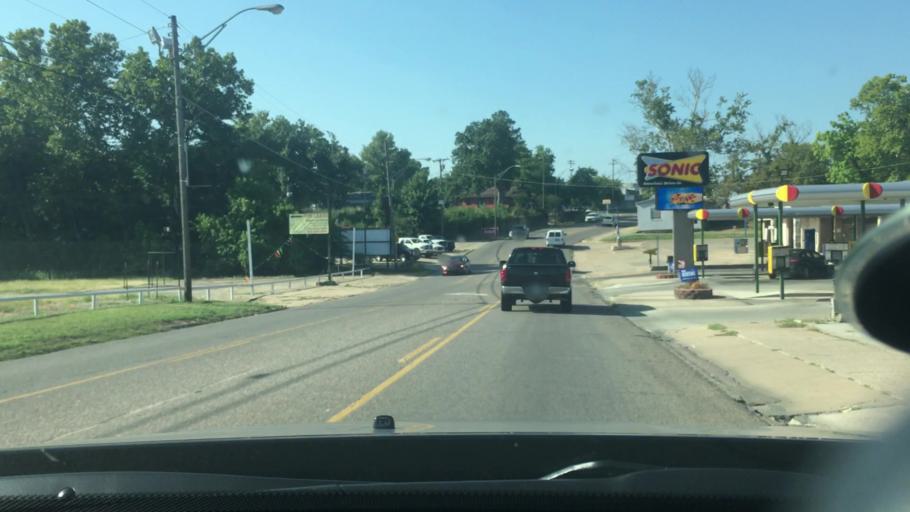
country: US
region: Oklahoma
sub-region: Bryan County
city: Durant
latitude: 34.0016
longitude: -96.3730
